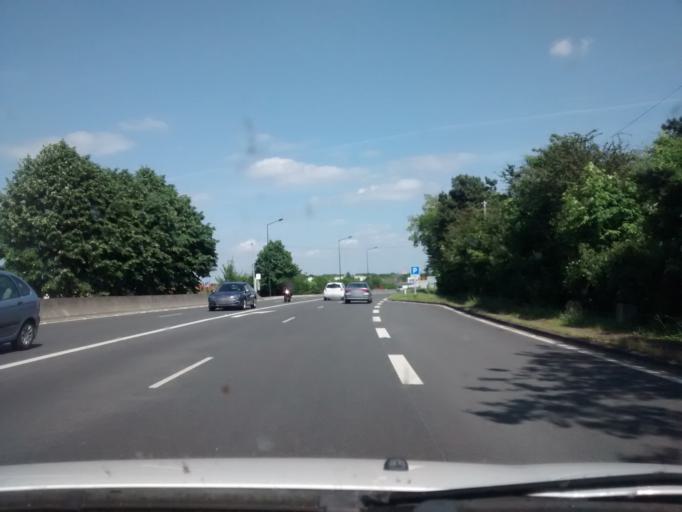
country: FR
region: Ile-de-France
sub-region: Departement des Yvelines
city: Saint-Cyr-l'Ecole
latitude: 48.7956
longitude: 2.0587
